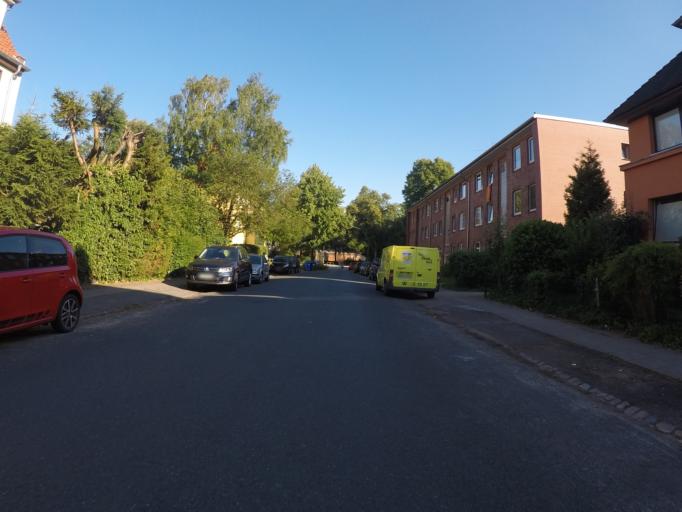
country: DE
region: Hamburg
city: Fuhlsbuettel
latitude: 53.6245
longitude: 10.0184
